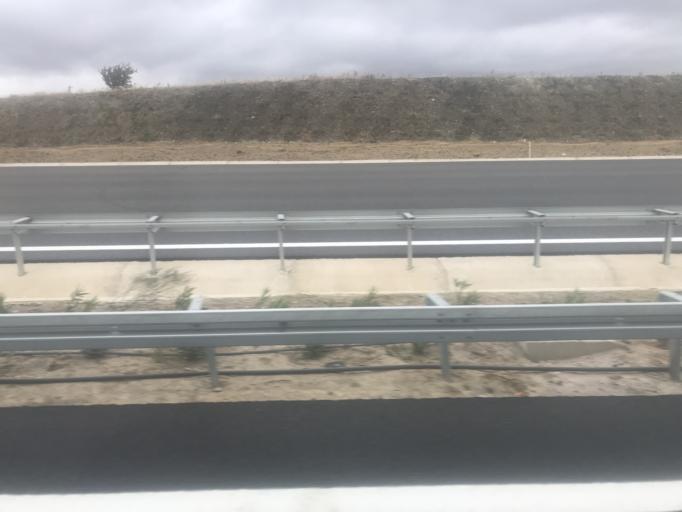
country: TR
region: Balikesir
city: Omerkoy
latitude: 39.8350
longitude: 28.0818
